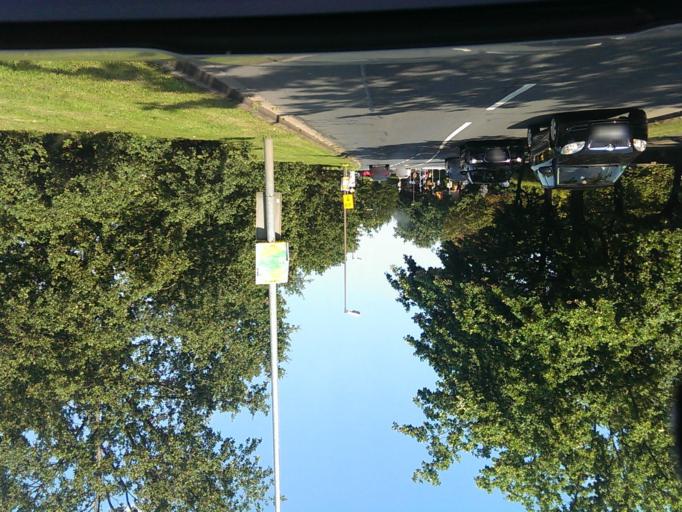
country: DE
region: Lower Saxony
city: Langenhagen
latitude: 52.4387
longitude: 9.7544
